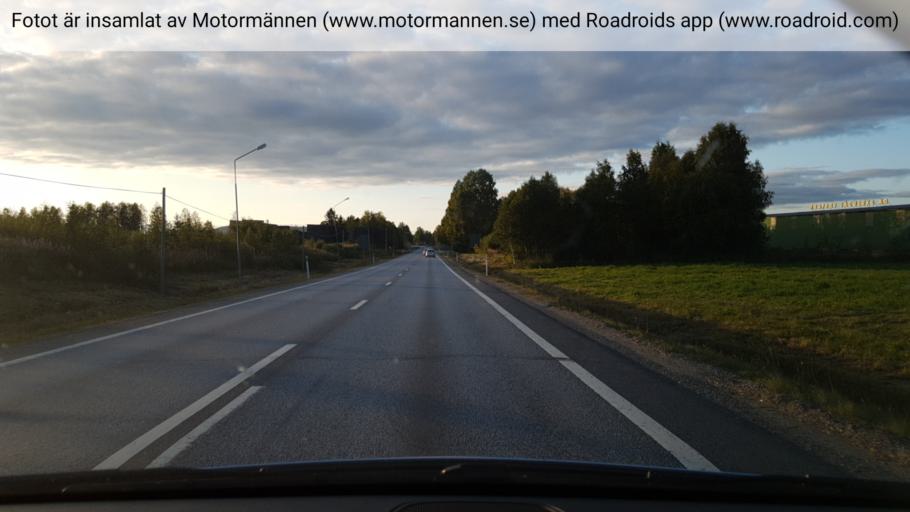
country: SE
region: Vaesterbotten
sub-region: Vannas Kommun
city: Vannasby
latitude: 63.9153
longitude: 19.8798
